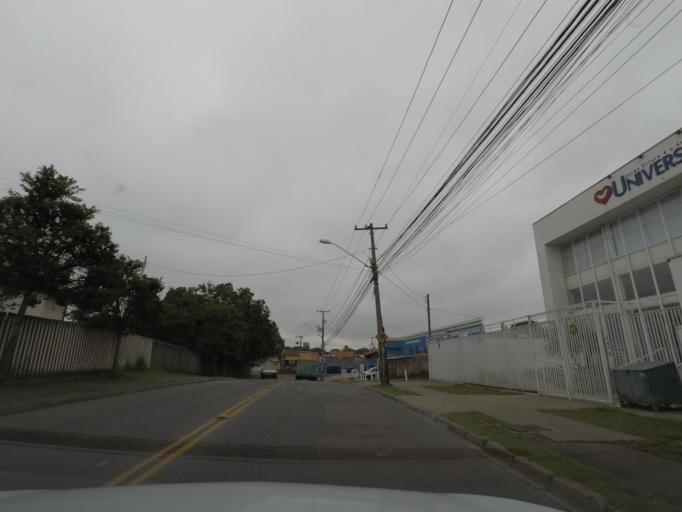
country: BR
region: Parana
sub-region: Curitiba
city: Curitiba
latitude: -25.4569
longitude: -49.3474
